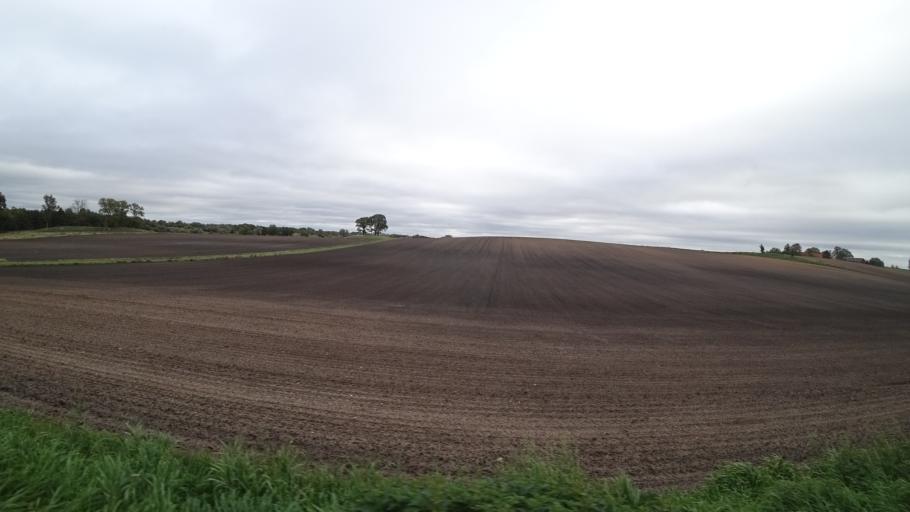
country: SE
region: Skane
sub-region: Kavlinge Kommun
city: Kaevlinge
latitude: 55.7881
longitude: 13.1384
